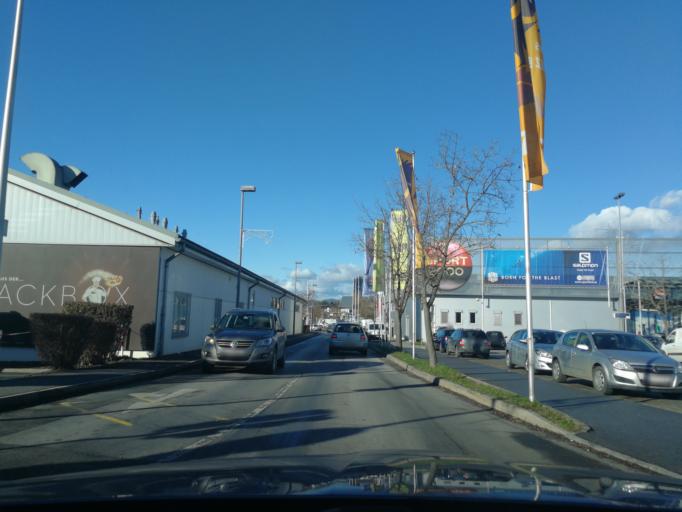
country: AT
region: Styria
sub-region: Politischer Bezirk Weiz
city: Gleisdorf
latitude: 47.1058
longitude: 15.7060
